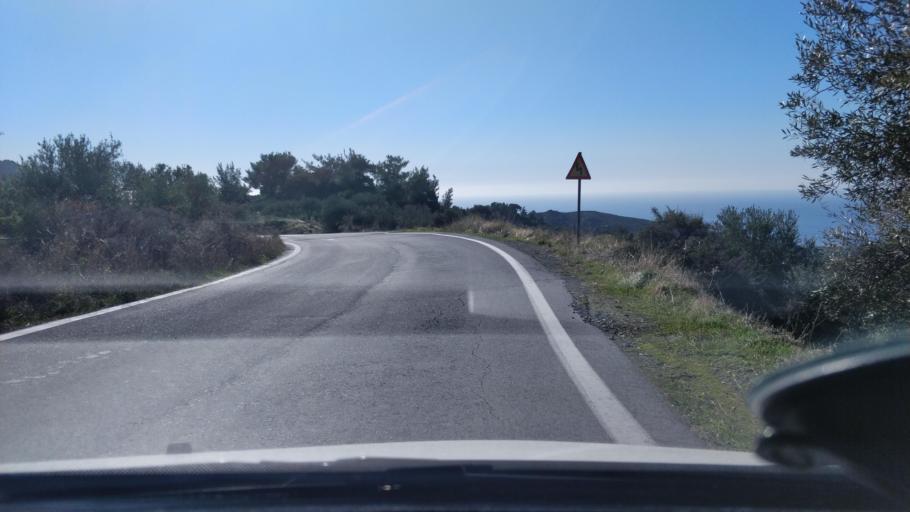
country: GR
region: Crete
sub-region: Nomos Irakleiou
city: Kastelli
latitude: 35.0301
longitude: 25.4491
